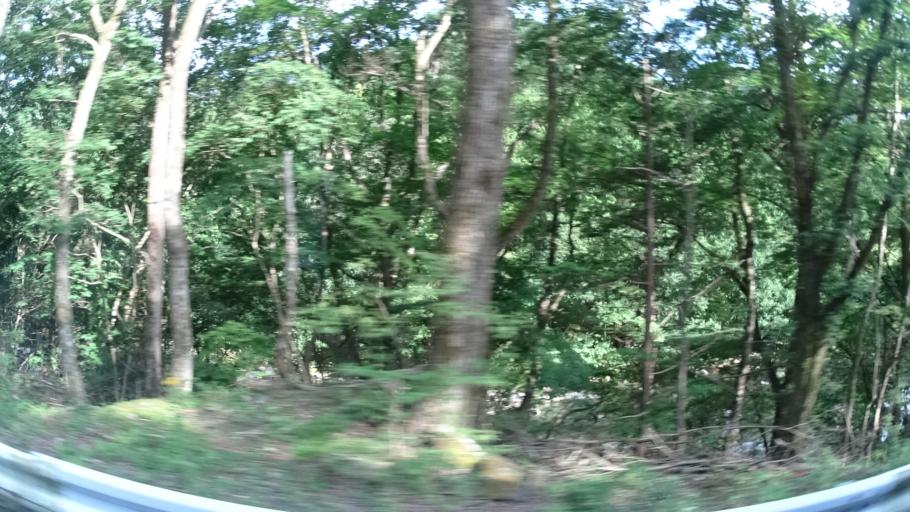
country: JP
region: Tochigi
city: Nikko
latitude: 36.6687
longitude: 139.4764
